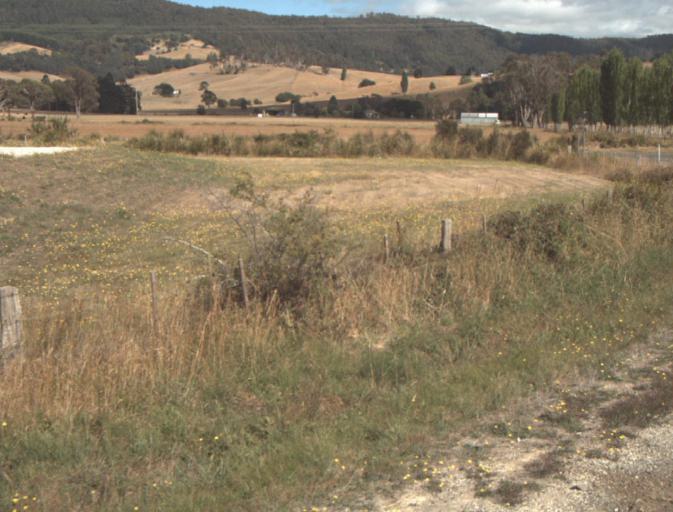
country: AU
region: Tasmania
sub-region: Launceston
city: Mayfield
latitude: -41.2531
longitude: 147.1478
